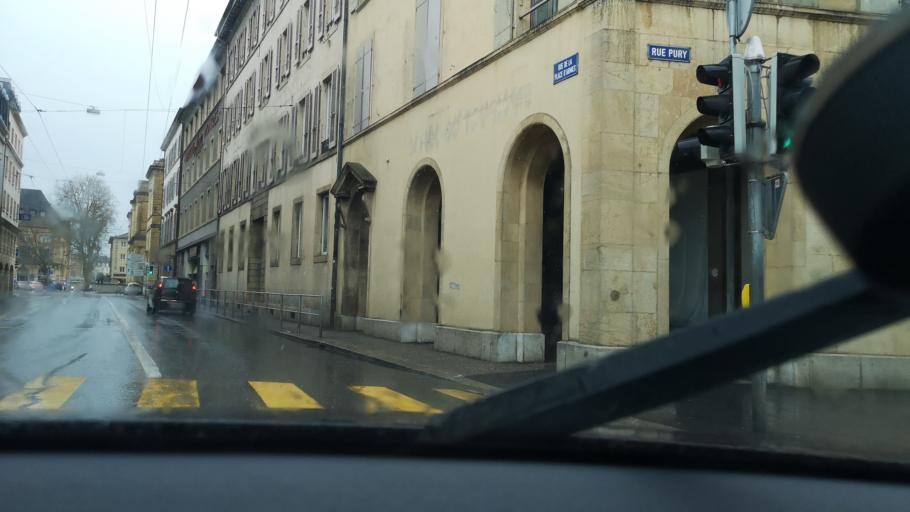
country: CH
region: Neuchatel
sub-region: Neuchatel District
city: Neuchatel
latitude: 46.9896
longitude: 6.9297
